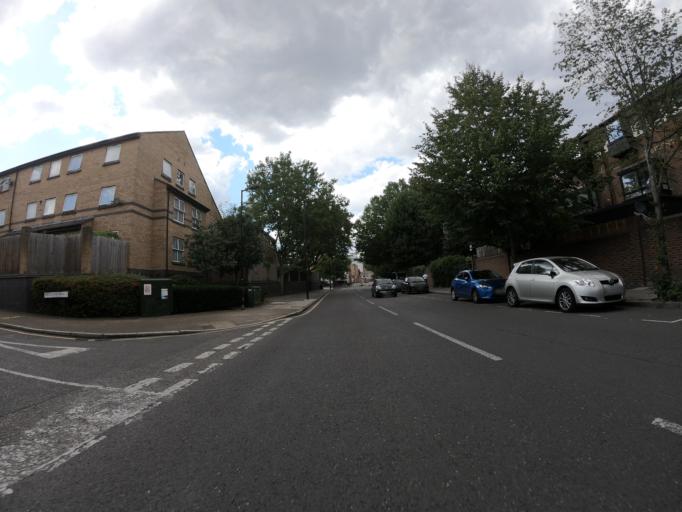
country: GB
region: England
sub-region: Greater London
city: Poplar
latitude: 51.4896
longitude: -0.0226
